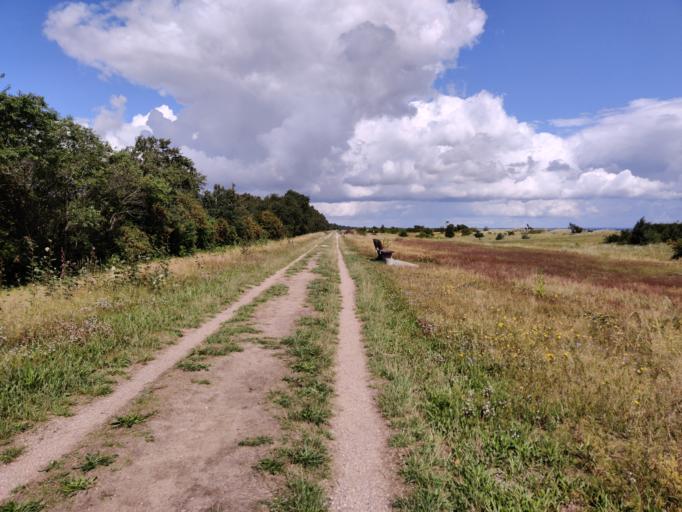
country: DK
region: Zealand
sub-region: Guldborgsund Kommune
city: Nykobing Falster
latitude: 54.6401
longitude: 11.9608
